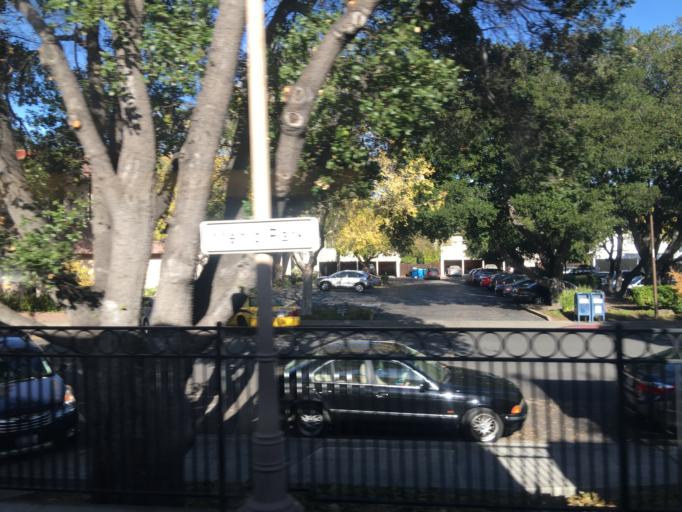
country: US
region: California
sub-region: San Mateo County
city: Menlo Park
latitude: 37.4547
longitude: -122.1820
